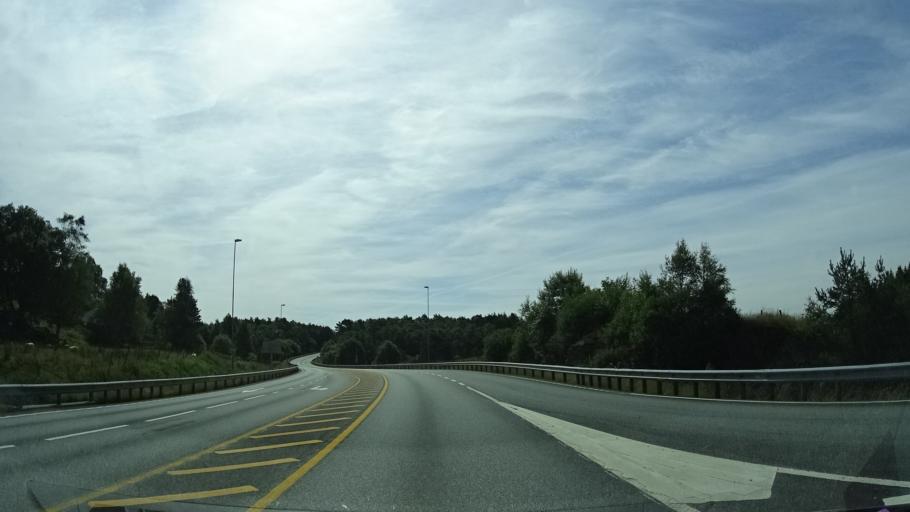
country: NO
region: Hordaland
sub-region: Sveio
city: Sveio
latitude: 59.5614
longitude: 5.4156
